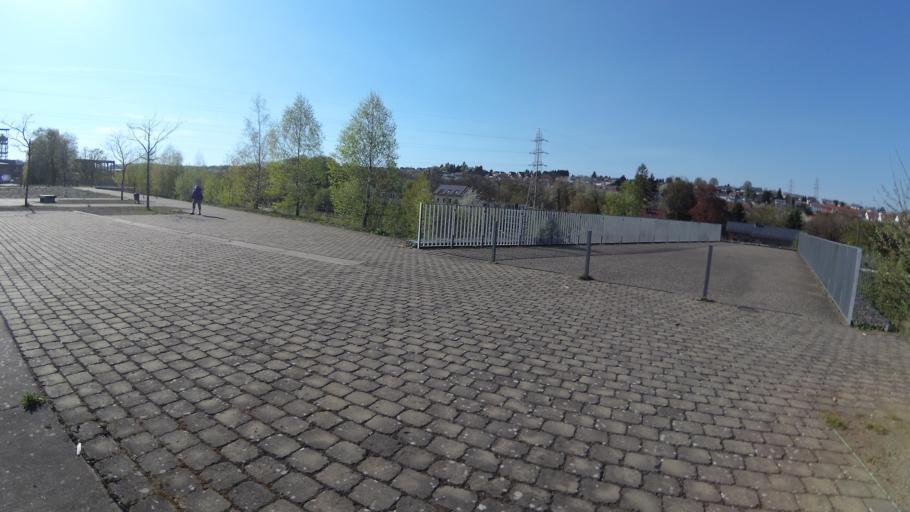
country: DE
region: Saarland
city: Schiffweiler
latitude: 49.3516
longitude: 7.1194
